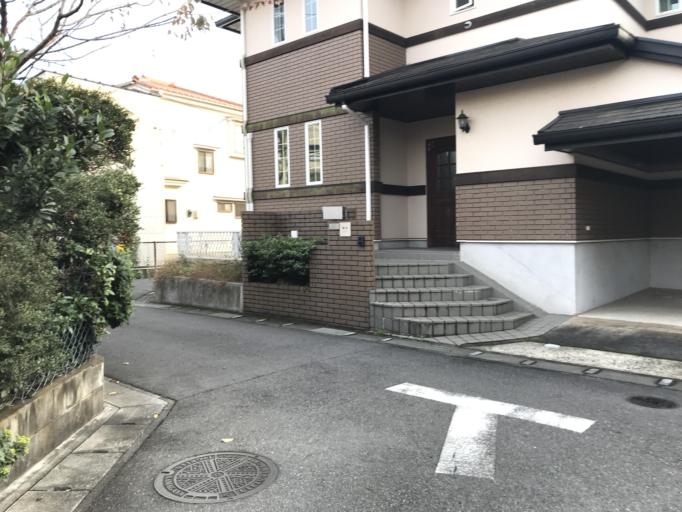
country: JP
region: Chiba
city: Shiroi
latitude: 35.7760
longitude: 140.0054
